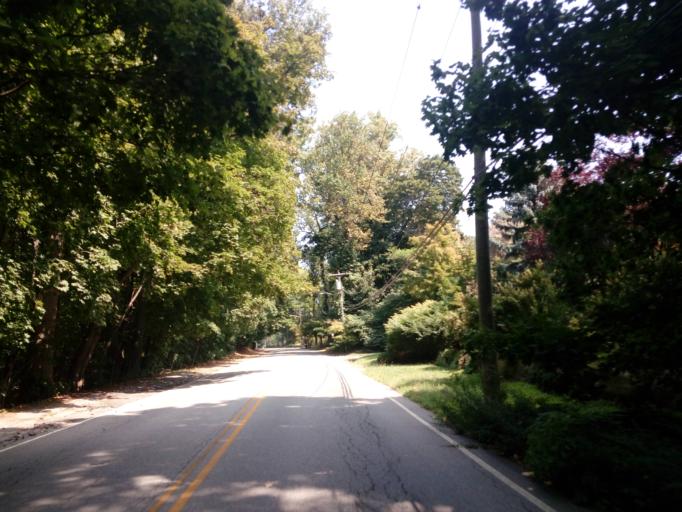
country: US
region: New York
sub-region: Nassau County
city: Glen Cove
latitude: 40.8783
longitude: -73.6402
